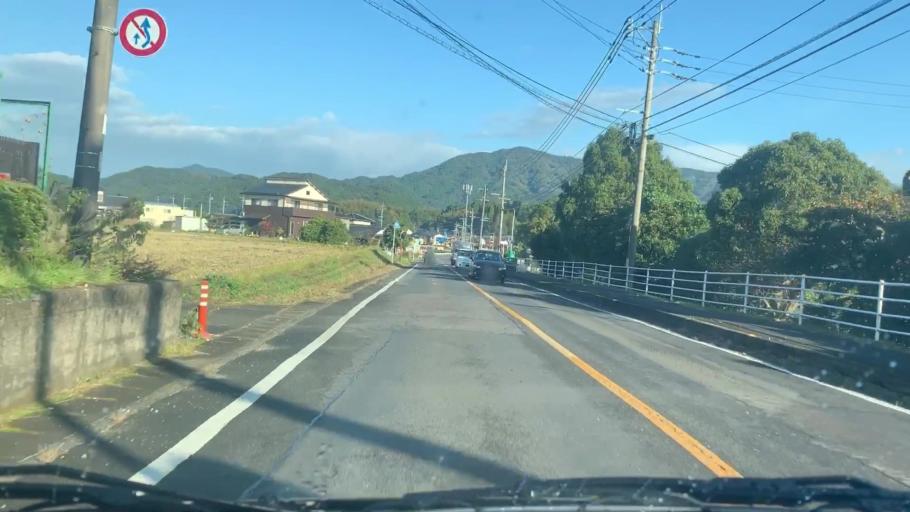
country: JP
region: Saga Prefecture
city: Takeocho-takeo
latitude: 33.2178
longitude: 130.0283
